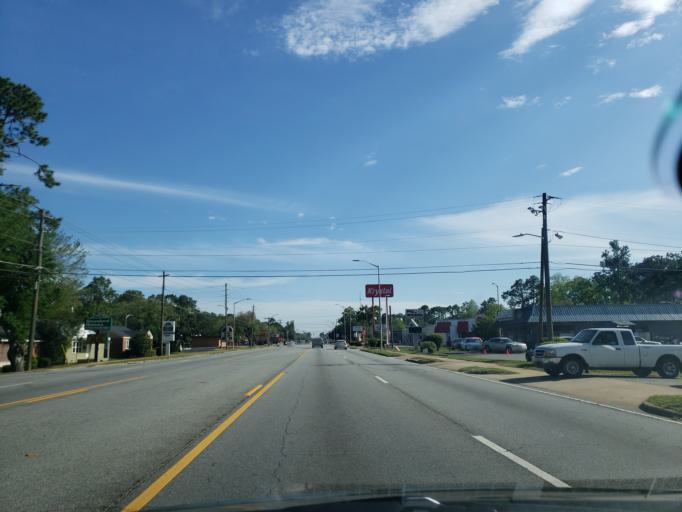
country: US
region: Georgia
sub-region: Dougherty County
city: Albany
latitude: 31.6001
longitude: -84.1760
